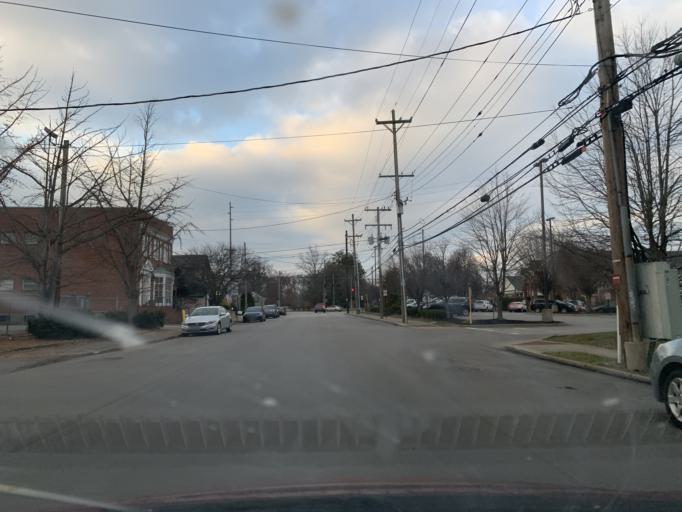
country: US
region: Kentucky
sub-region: Jefferson County
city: Saint Matthews
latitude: 38.2525
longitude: -85.6616
